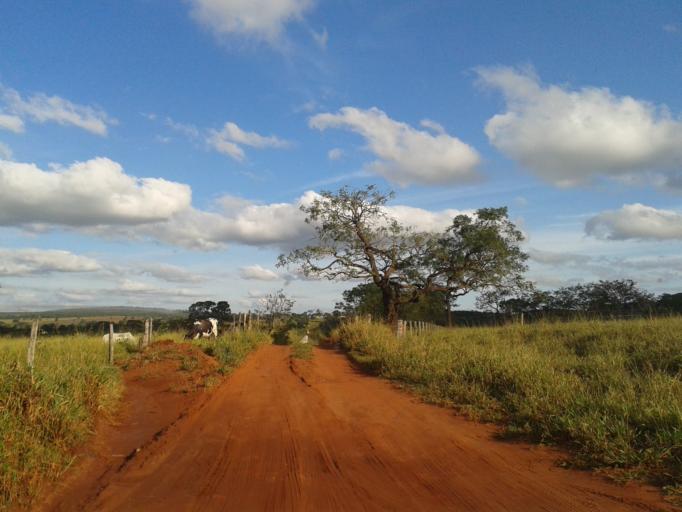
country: BR
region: Minas Gerais
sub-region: Campina Verde
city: Campina Verde
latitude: -19.4109
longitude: -49.7456
